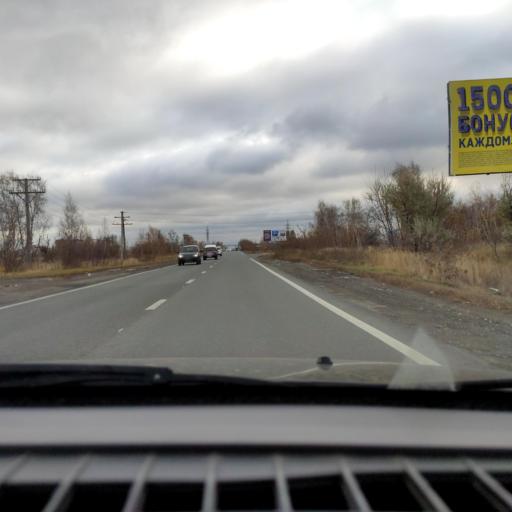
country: RU
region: Samara
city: Tol'yatti
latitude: 53.5491
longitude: 49.3747
